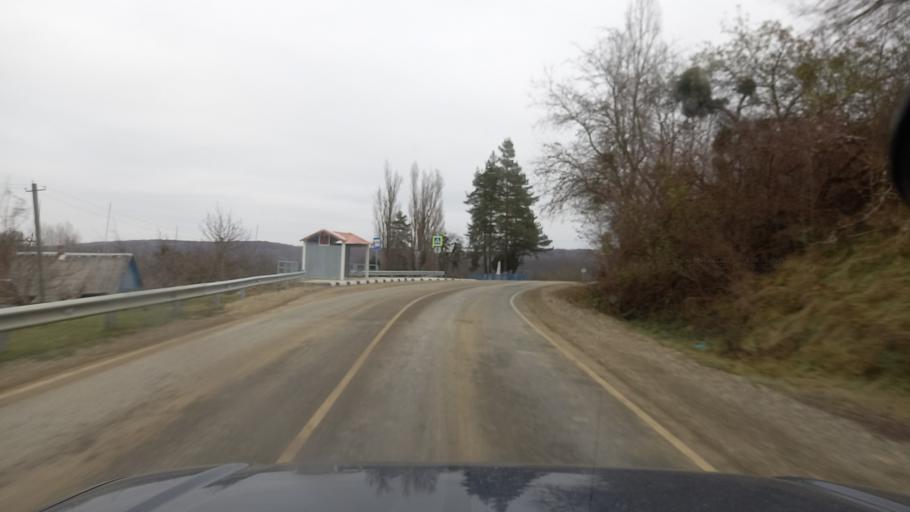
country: RU
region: Krasnodarskiy
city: Saratovskaya
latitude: 44.5462
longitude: 39.2881
